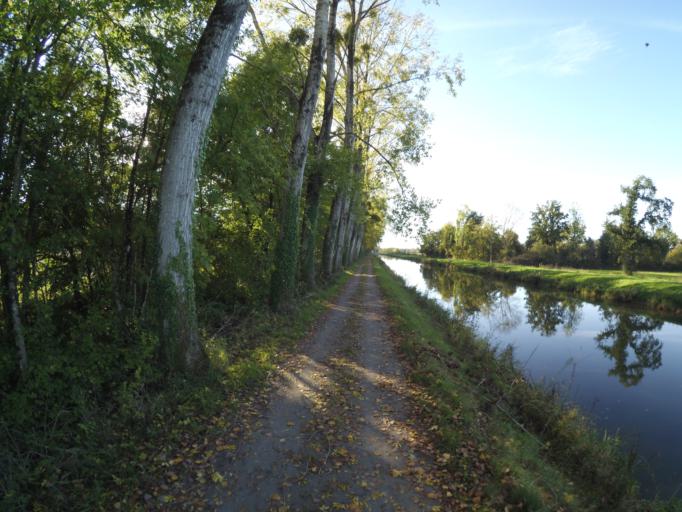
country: FR
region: Brittany
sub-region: Departement du Morbihan
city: Saint-Vincent-sur-Oust
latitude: 47.7179
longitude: -2.1523
